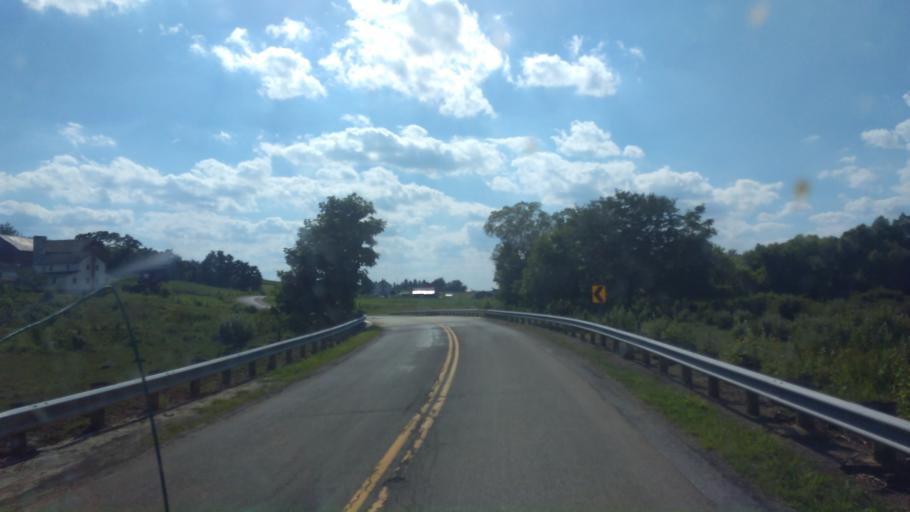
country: US
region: Ohio
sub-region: Wayne County
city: Dalton
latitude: 40.7540
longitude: -81.6748
